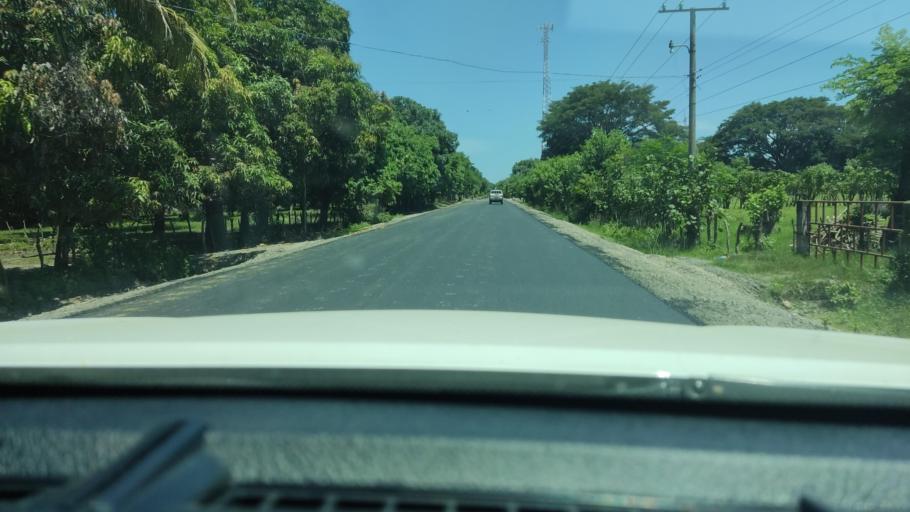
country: SV
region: Ahuachapan
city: San Francisco Menendez
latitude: 13.8298
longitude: -90.1189
